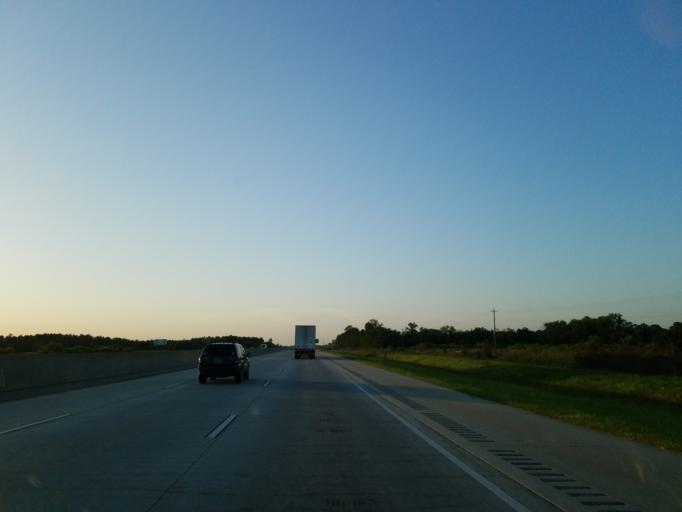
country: US
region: Georgia
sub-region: Tift County
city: Unionville
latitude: 31.3417
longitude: -83.4857
